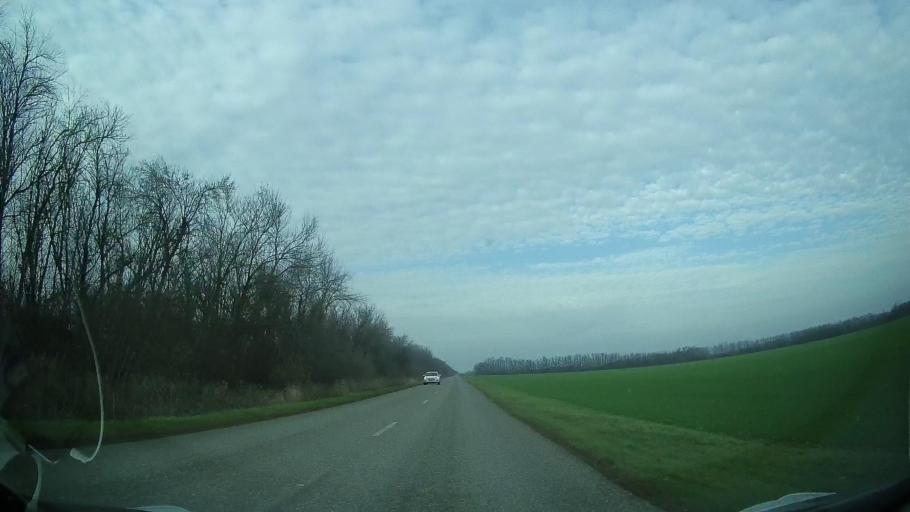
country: RU
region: Rostov
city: Zernograd
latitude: 46.9828
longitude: 40.3916
